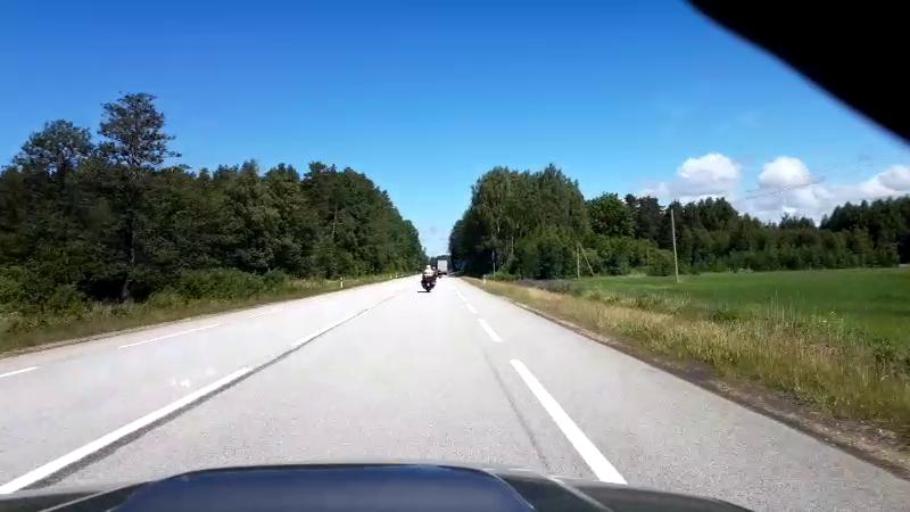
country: LV
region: Saulkrastu
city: Saulkrasti
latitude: 57.4291
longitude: 24.4295
